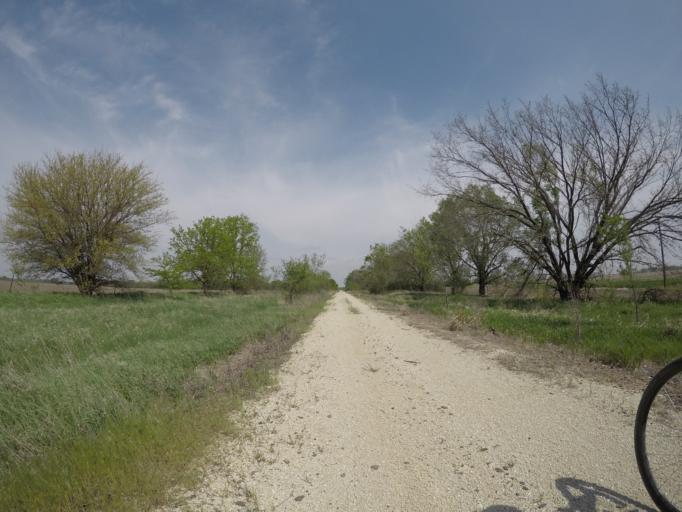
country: US
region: Nebraska
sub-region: Gage County
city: Wymore
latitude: 40.1623
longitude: -96.6434
